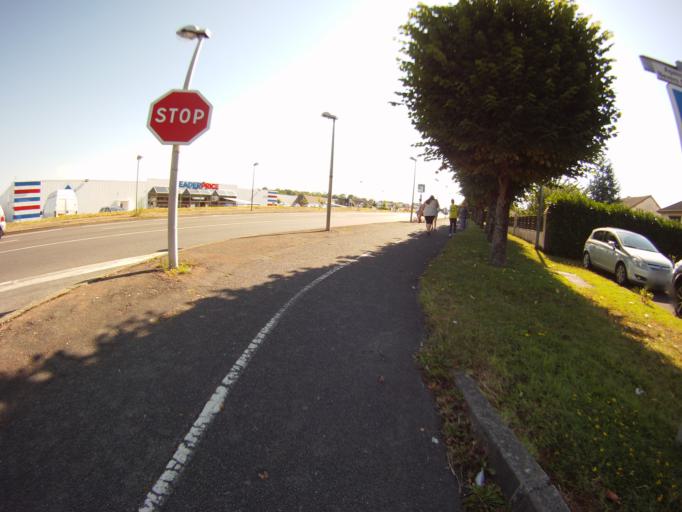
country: FR
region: Bourgogne
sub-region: Departement de la Nievre
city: Varennes-Vauzelles
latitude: 46.9961
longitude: 3.1244
